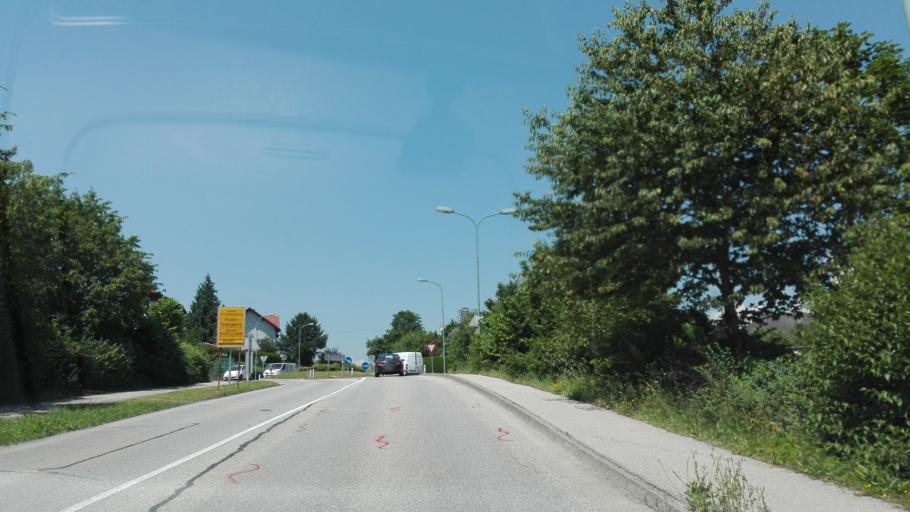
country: AT
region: Upper Austria
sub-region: Politischer Bezirk Linz-Land
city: Pasching
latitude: 48.2717
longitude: 14.2008
